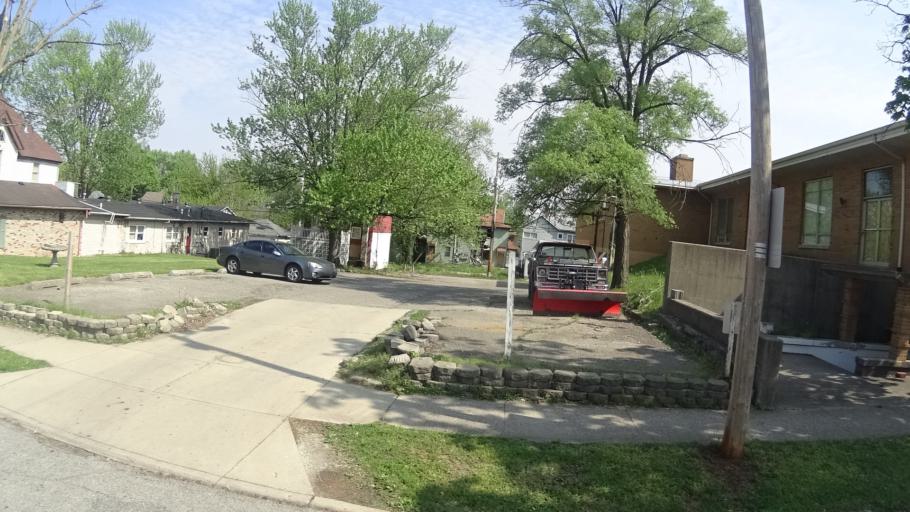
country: US
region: Indiana
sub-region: Madison County
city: Anderson
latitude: 40.1051
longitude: -85.6836
